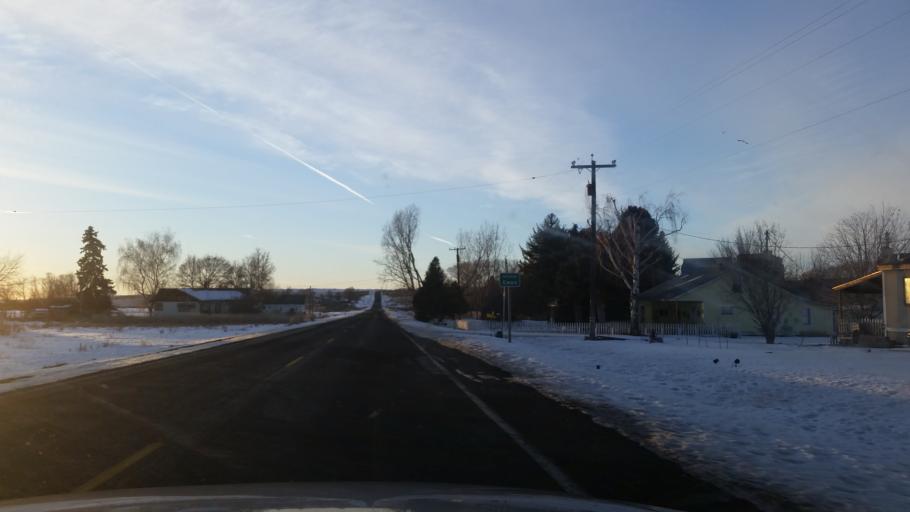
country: US
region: Washington
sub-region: Spokane County
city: Cheney
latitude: 47.1170
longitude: -117.7255
